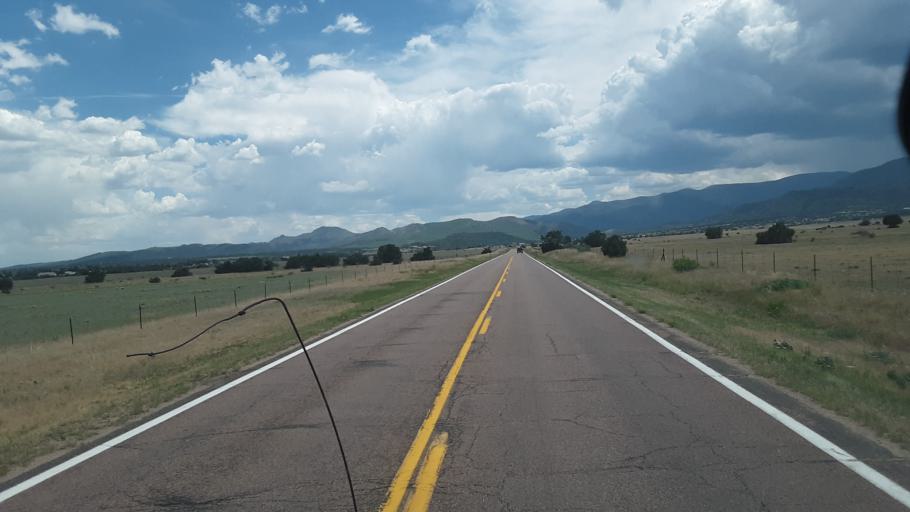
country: US
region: Colorado
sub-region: Fremont County
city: Florence
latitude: 38.2673
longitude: -105.0874
